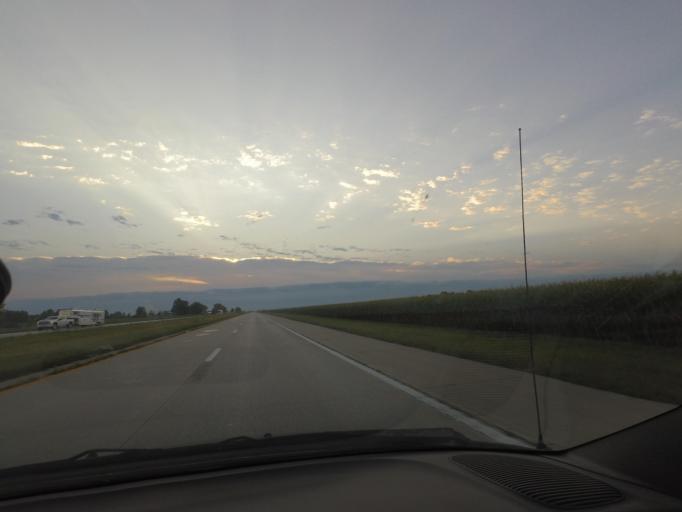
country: US
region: Missouri
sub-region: Macon County
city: Macon
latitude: 39.7501
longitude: -92.3413
